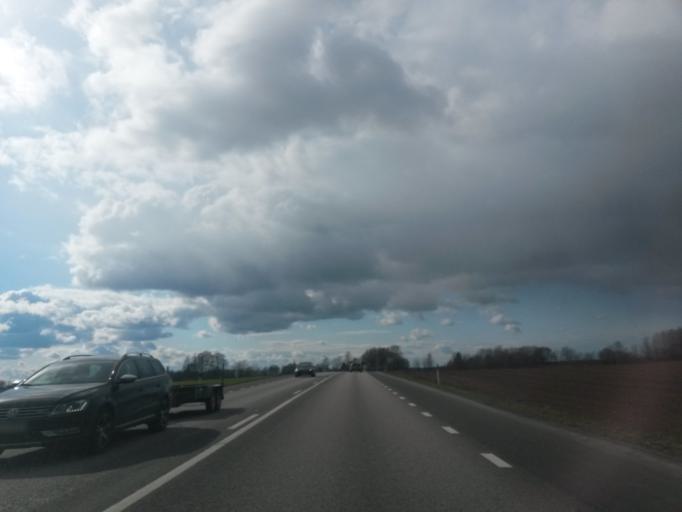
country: SE
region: Vaestra Goetaland
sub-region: Skara Kommun
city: Axvall
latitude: 58.3832
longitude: 13.6713
